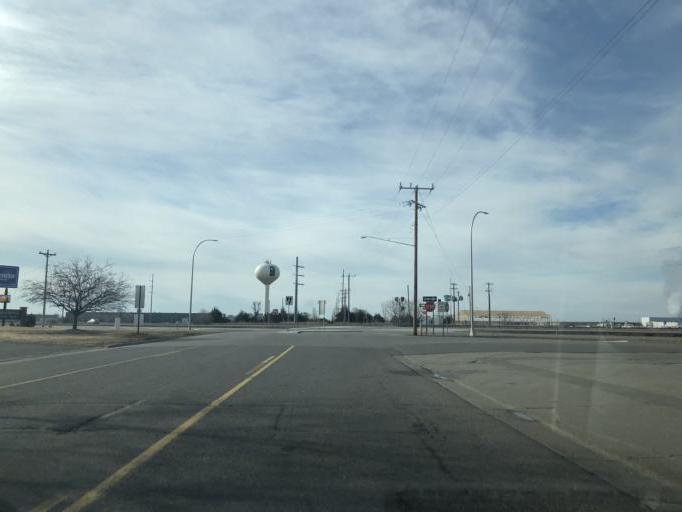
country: US
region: Minnesota
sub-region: Sherburne County
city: Becker
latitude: 45.3895
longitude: -93.8704
